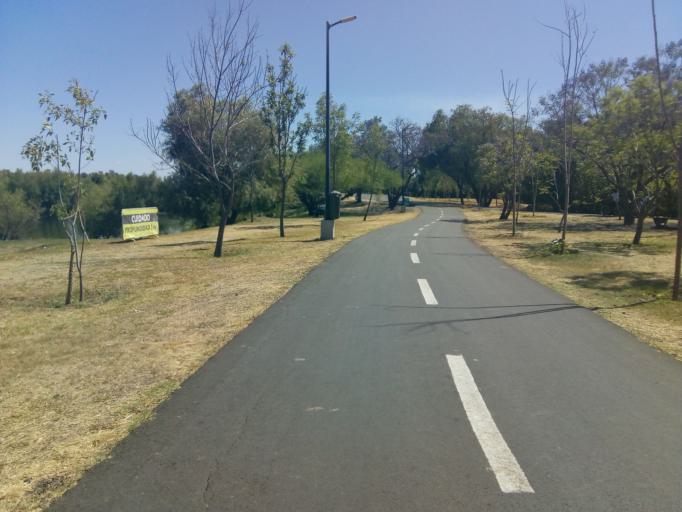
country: MX
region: Guanajuato
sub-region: Leon
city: La Ermita
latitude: 21.1814
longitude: -101.6961
